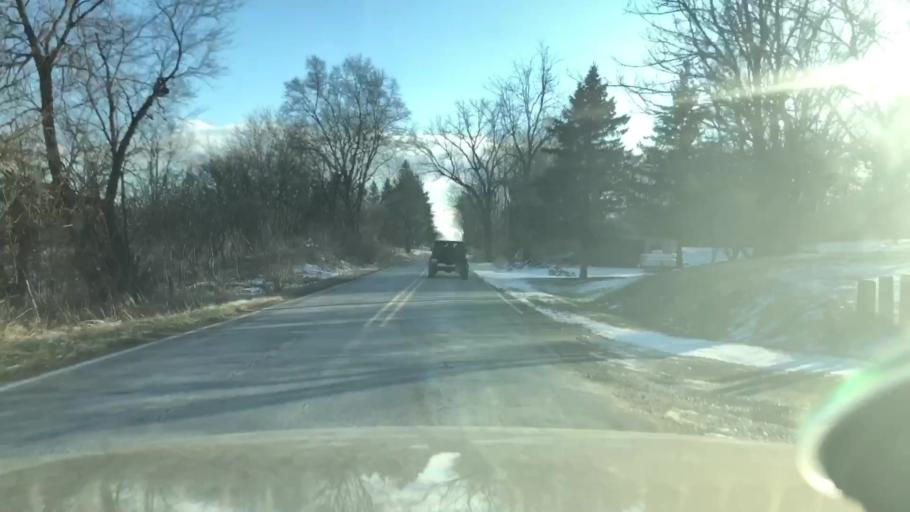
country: US
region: Michigan
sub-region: Jackson County
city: Vandercook Lake
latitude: 42.1238
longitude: -84.4515
